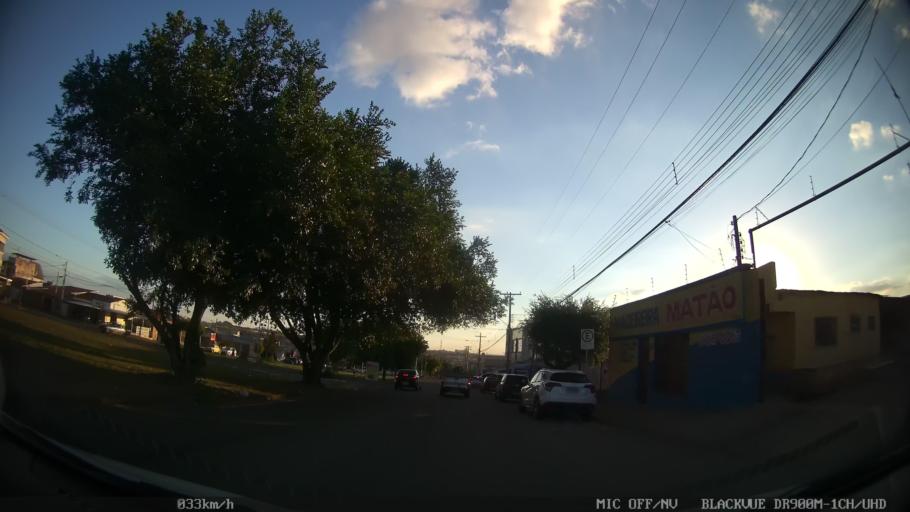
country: BR
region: Sao Paulo
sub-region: Santa Barbara D'Oeste
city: Santa Barbara d'Oeste
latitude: -22.7339
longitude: -47.3870
